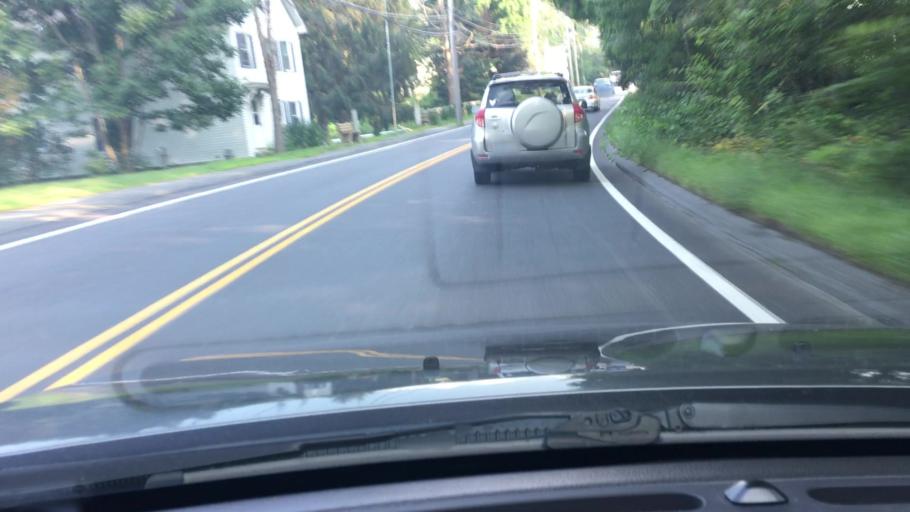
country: US
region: Massachusetts
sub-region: Middlesex County
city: Hopkinton
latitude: 42.2402
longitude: -71.5667
